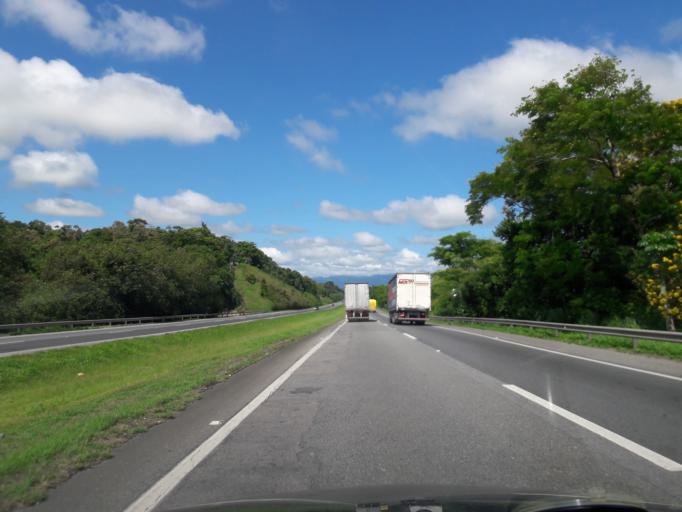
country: BR
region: Sao Paulo
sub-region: Jacupiranga
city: Jacupiranga
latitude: -24.6572
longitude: -47.9660
